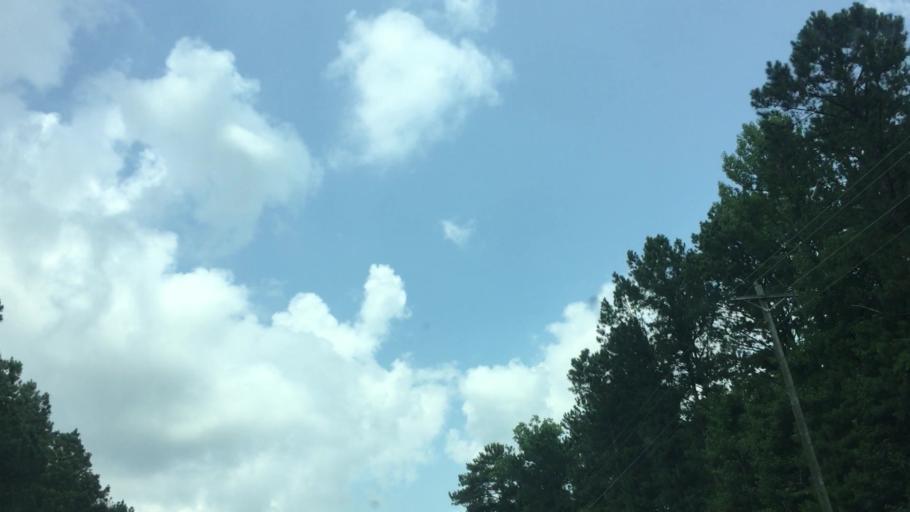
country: US
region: Georgia
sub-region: Fulton County
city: Chattahoochee Hills
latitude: 33.5833
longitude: -84.8205
